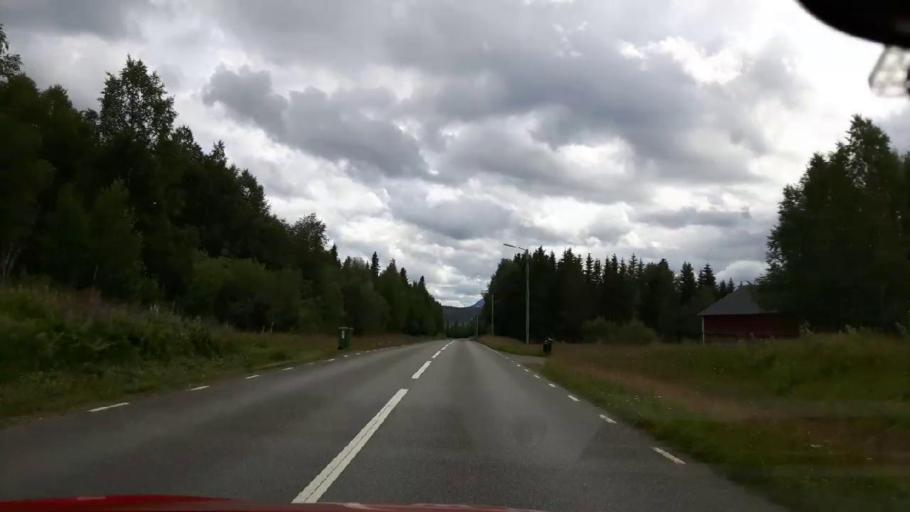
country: NO
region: Nord-Trondelag
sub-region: Lierne
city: Sandvika
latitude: 64.3936
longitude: 14.3680
